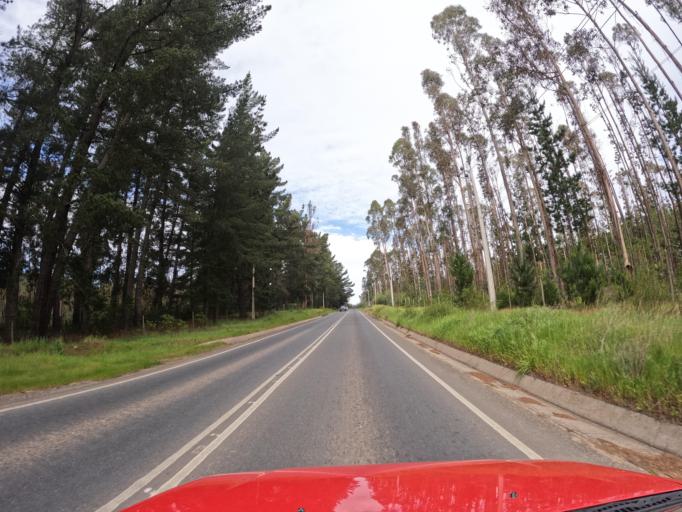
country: CL
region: O'Higgins
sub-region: Provincia de Colchagua
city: Santa Cruz
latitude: -34.3571
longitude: -71.8737
